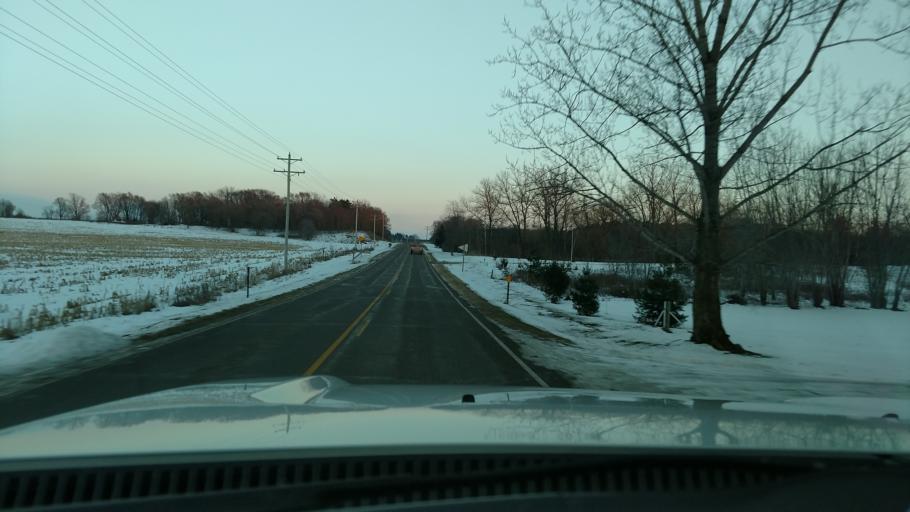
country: US
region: Wisconsin
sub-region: Saint Croix County
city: Roberts
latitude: 44.9135
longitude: -92.5275
